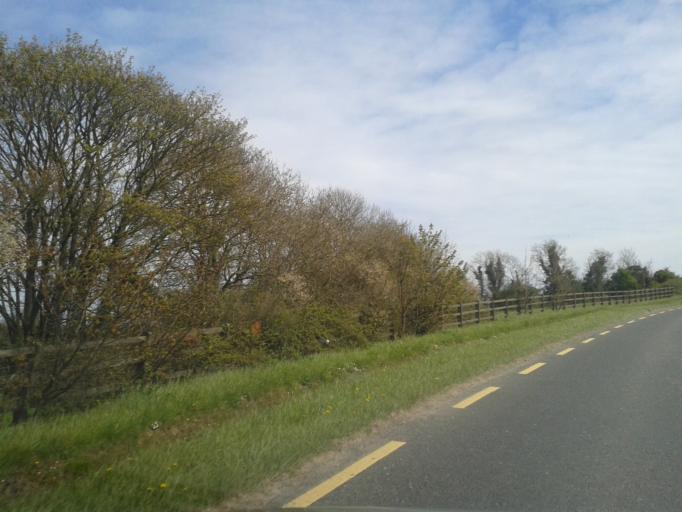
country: IE
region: Leinster
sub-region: Fingal County
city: Swords
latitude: 53.4372
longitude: -6.2387
